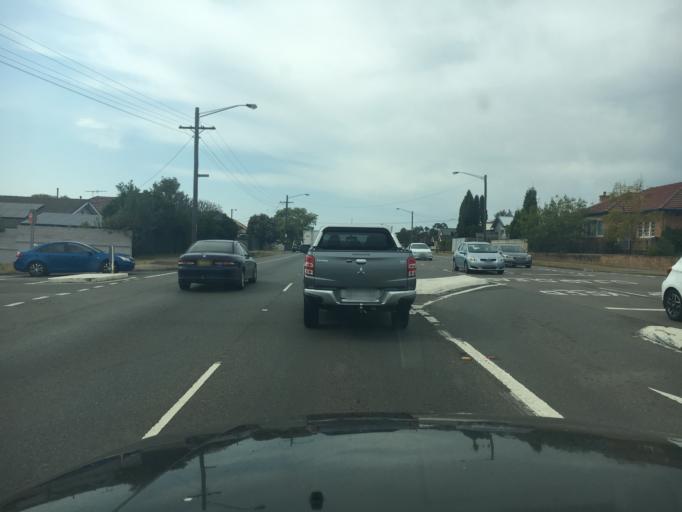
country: AU
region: New South Wales
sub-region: Maitland Municipality
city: East Maitland
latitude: -32.7544
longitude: 151.5882
